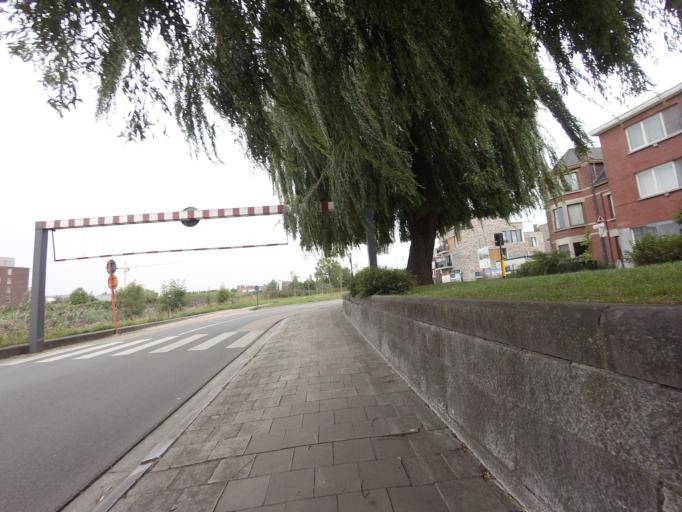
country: BE
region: Flanders
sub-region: Provincie Oost-Vlaanderen
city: Ledeberg
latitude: 51.0470
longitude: 3.7546
